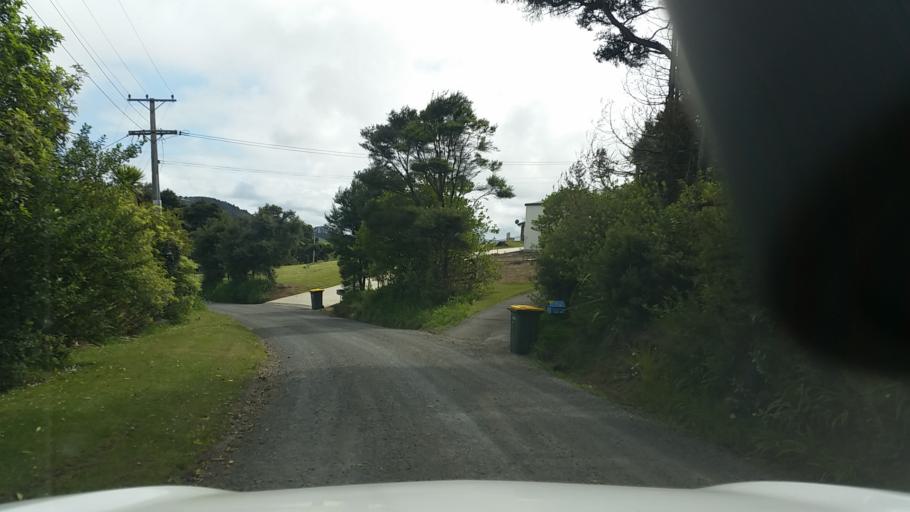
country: NZ
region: Auckland
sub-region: Auckland
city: Muriwai Beach
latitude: -36.8479
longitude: 174.5230
